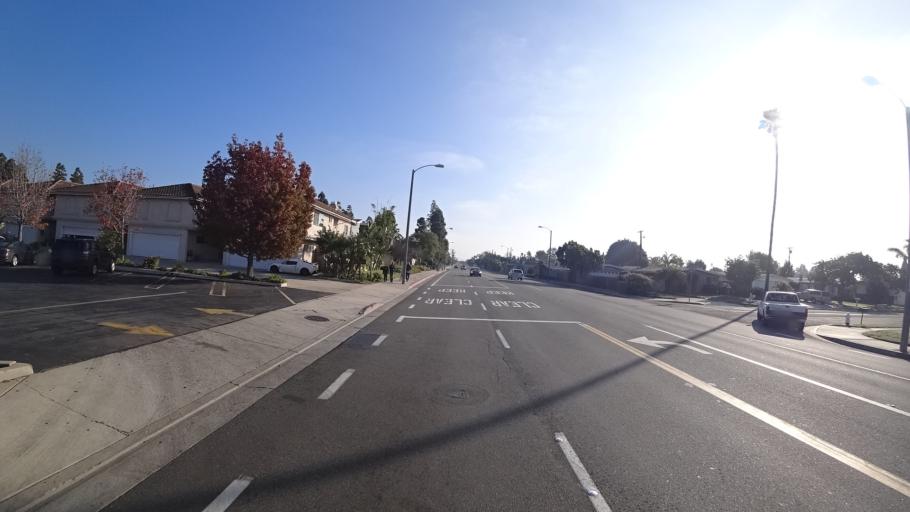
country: US
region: California
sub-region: Orange County
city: Costa Mesa
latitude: 33.6526
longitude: -117.9177
